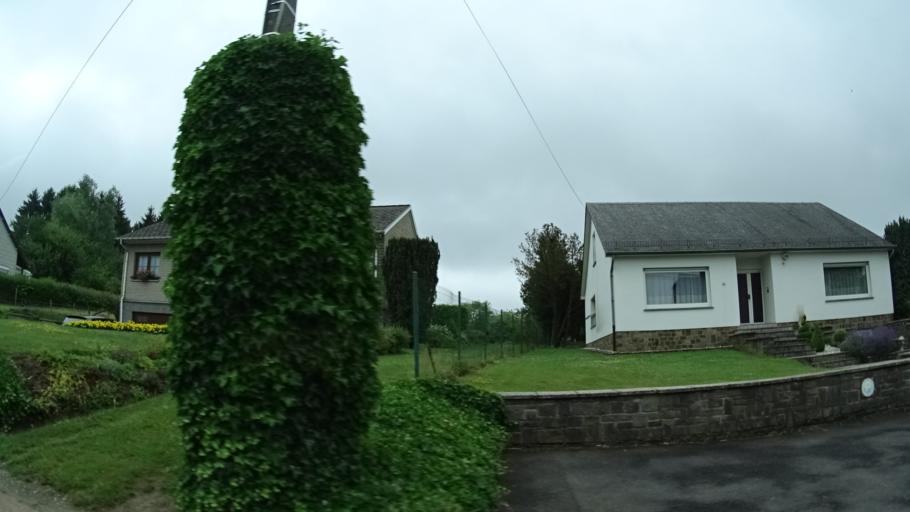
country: BE
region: Wallonia
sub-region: Province du Luxembourg
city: Habay-la-Vieille
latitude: 49.7235
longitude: 5.6284
